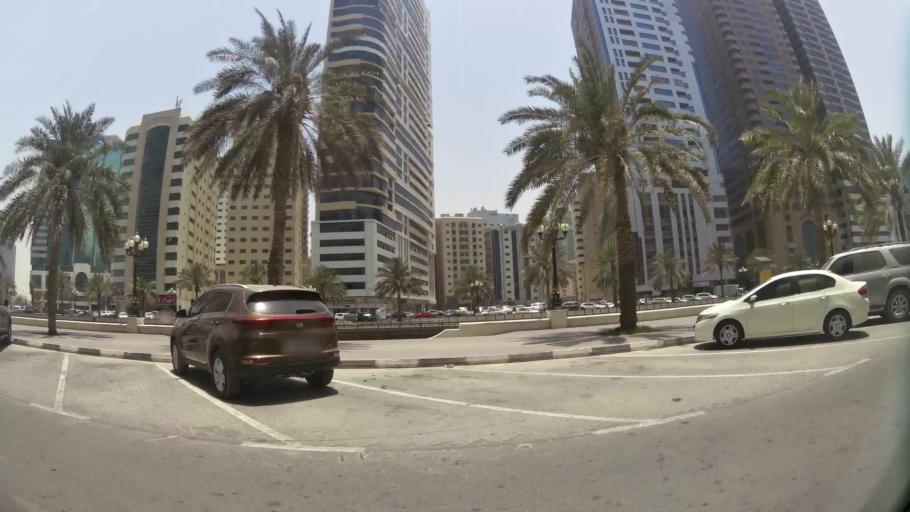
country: AE
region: Ash Shariqah
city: Sharjah
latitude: 25.3242
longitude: 55.3796
